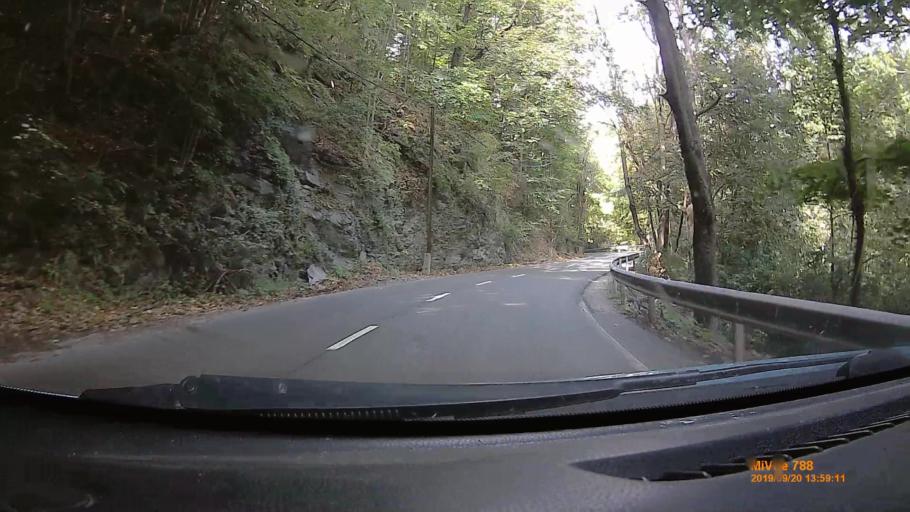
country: HU
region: Borsod-Abauj-Zemplen
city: Sajobabony
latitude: 48.1020
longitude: 20.6219
